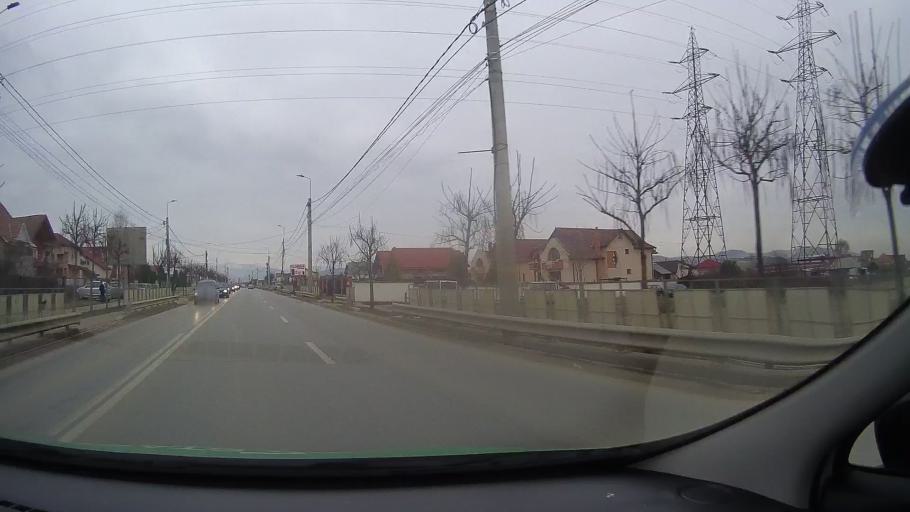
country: RO
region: Alba
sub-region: Municipiul Alba Iulia
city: Micesti
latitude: 46.0905
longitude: 23.5558
